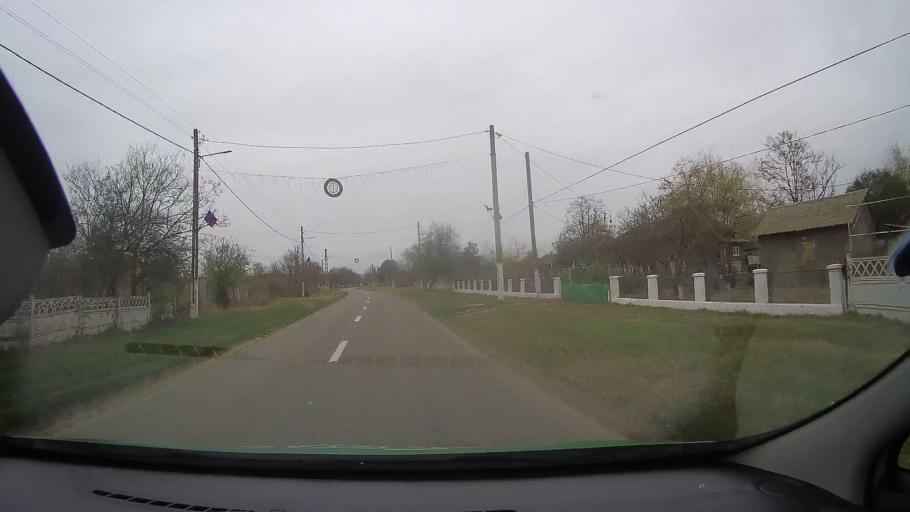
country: RO
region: Constanta
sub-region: Comuna Saraiu
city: Saraiu
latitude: 44.7208
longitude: 28.1616
